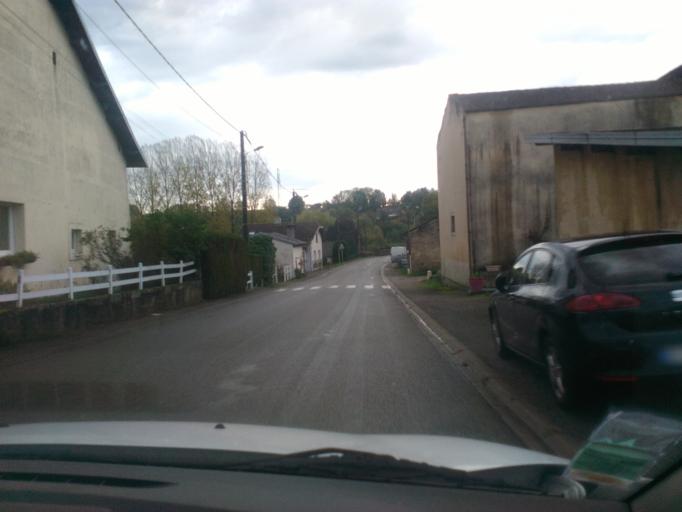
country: FR
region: Lorraine
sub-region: Departement des Vosges
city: Chavelot
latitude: 48.2828
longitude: 6.4711
